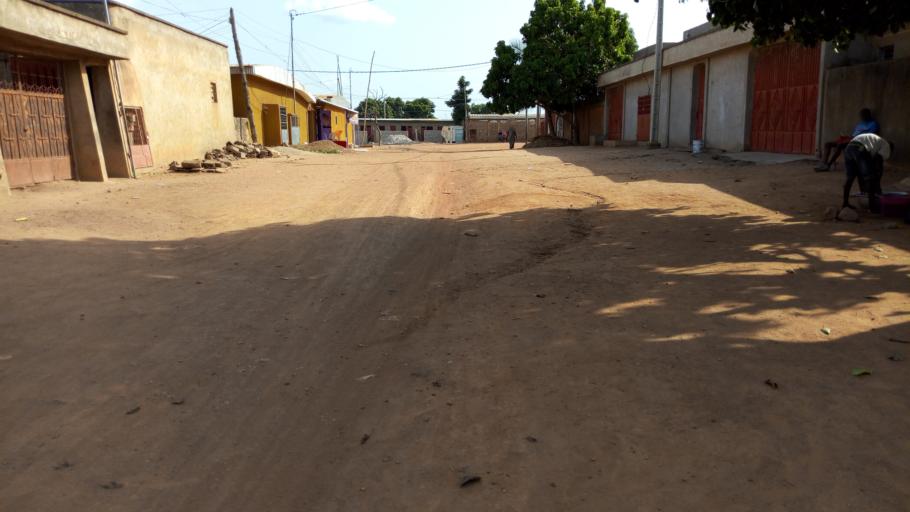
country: CI
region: Vallee du Bandama
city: Bouake
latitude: 7.7072
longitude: -5.0437
